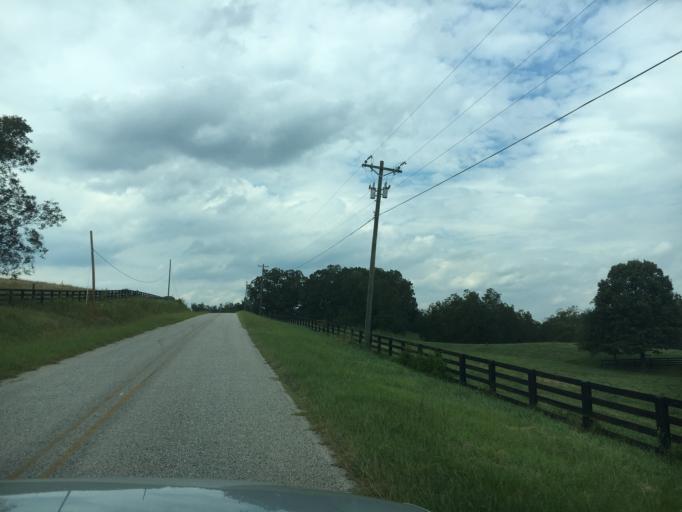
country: US
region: Georgia
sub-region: Franklin County
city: Gumlog
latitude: 34.4761
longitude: -83.0580
